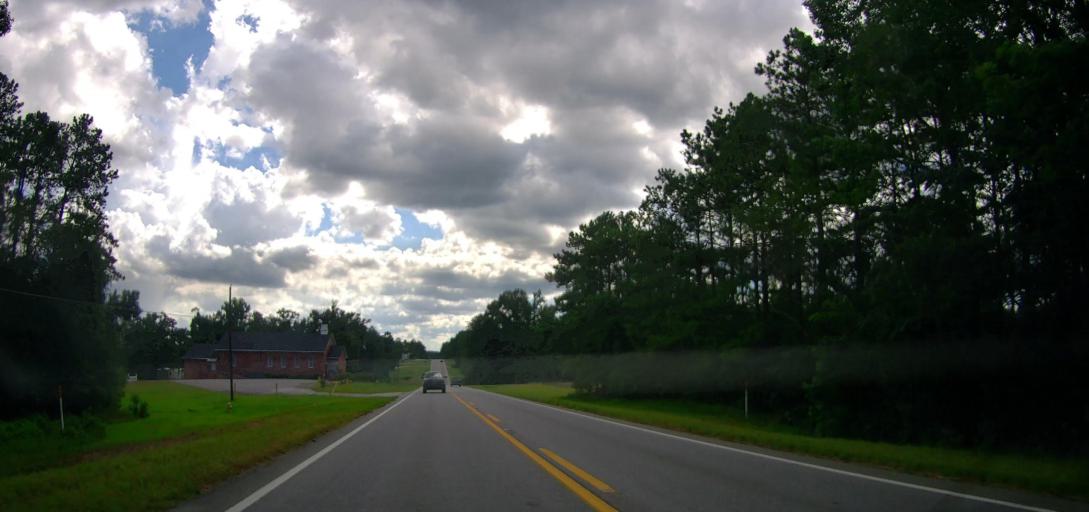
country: US
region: Alabama
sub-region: Russell County
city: Ladonia
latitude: 32.4551
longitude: -85.2005
